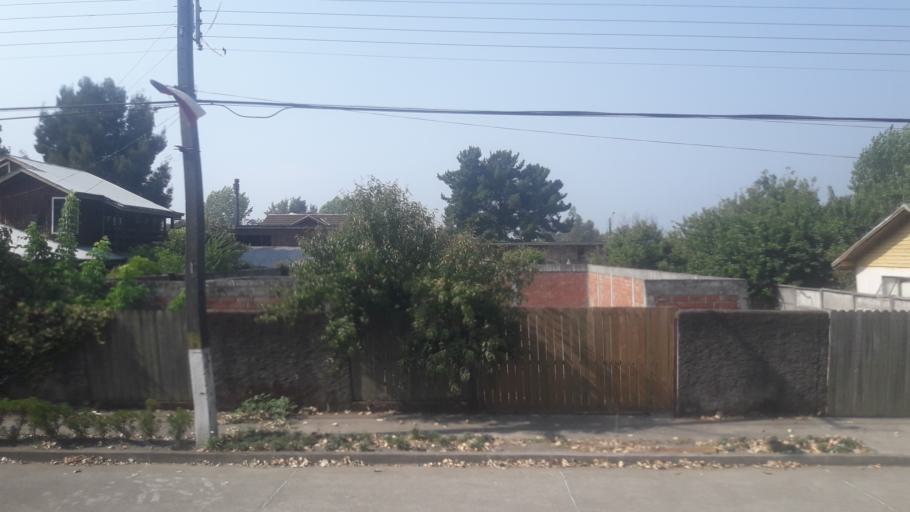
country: CL
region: Biobio
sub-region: Provincia de Concepcion
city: Lota
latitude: -37.1672
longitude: -72.9510
